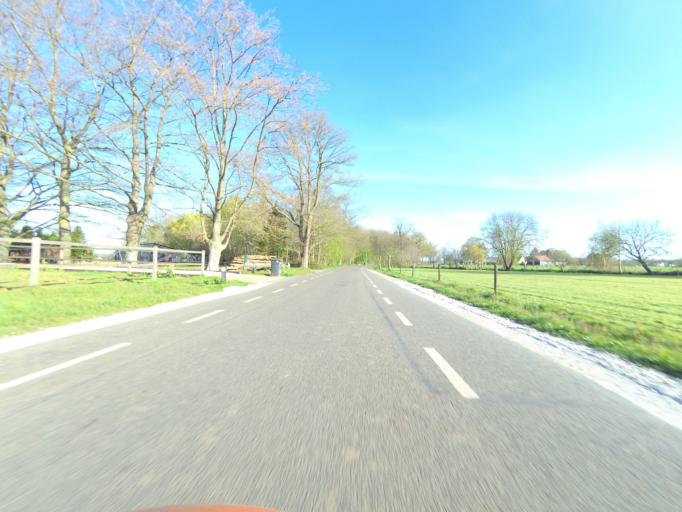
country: NL
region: Gelderland
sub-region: Gemeente Barneveld
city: Terschuur
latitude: 52.1532
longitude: 5.4970
